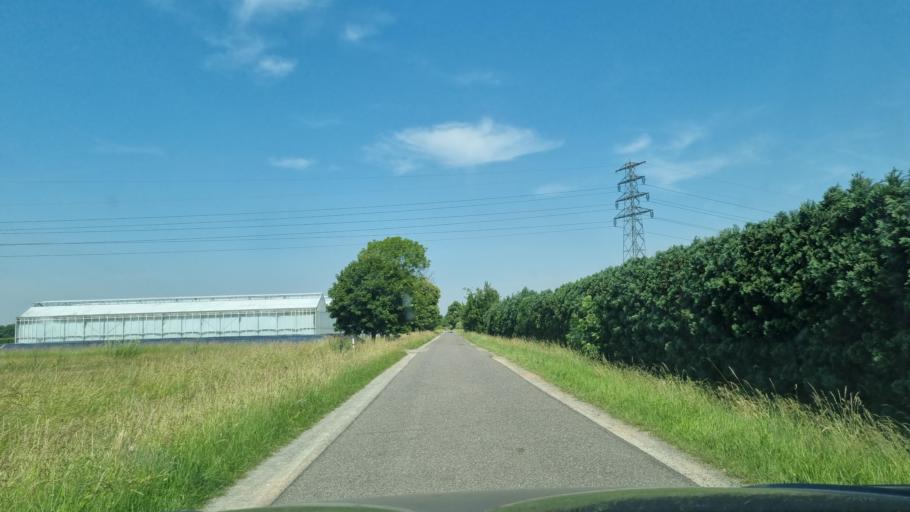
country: NL
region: Gelderland
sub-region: Gemeente Nijmegen
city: Nijmegen
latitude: 51.8829
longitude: 5.8749
